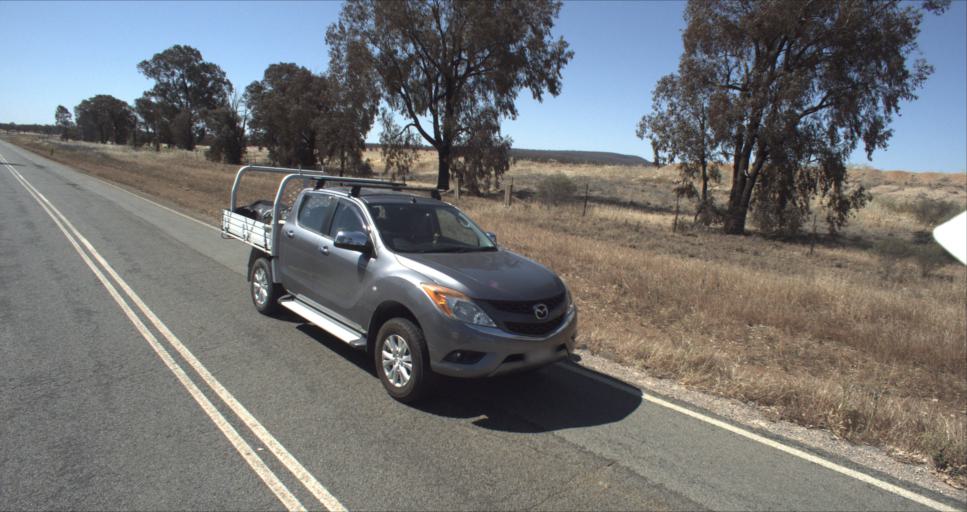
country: AU
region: New South Wales
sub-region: Leeton
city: Leeton
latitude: -34.4962
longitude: 146.4332
